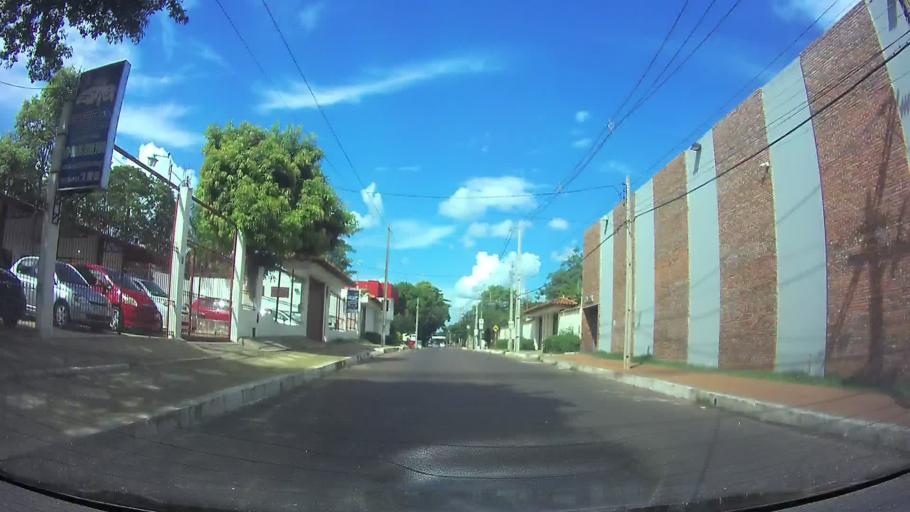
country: PY
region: Central
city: Villa Elisa
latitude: -25.3442
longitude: -57.5786
